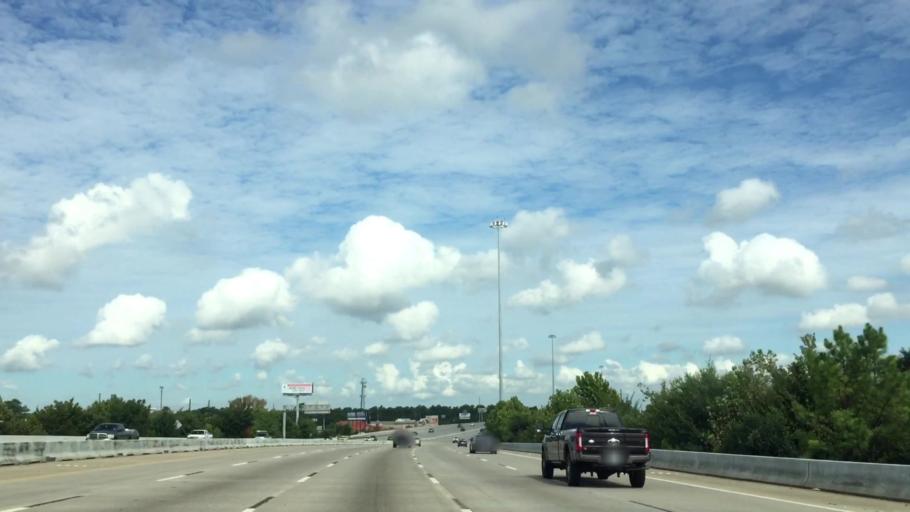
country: US
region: Texas
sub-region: Harris County
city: Oak Cliff Place
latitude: 29.9680
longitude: -95.5579
